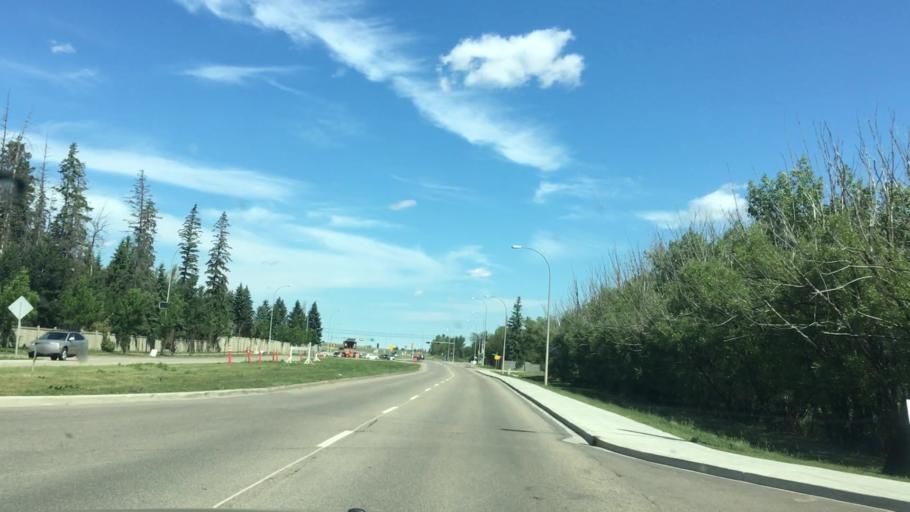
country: CA
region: Alberta
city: Beaumont
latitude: 53.4267
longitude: -113.5164
